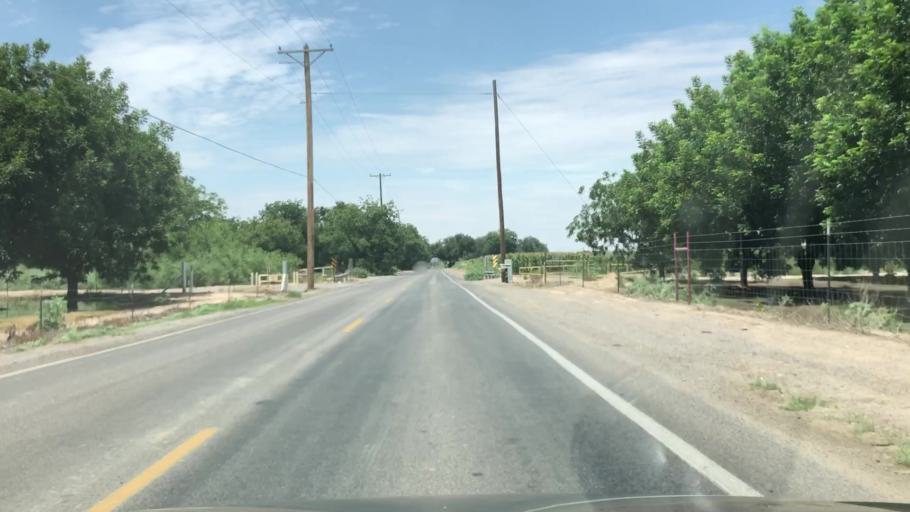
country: US
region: New Mexico
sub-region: Dona Ana County
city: Vado
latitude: 32.1117
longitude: -106.6789
